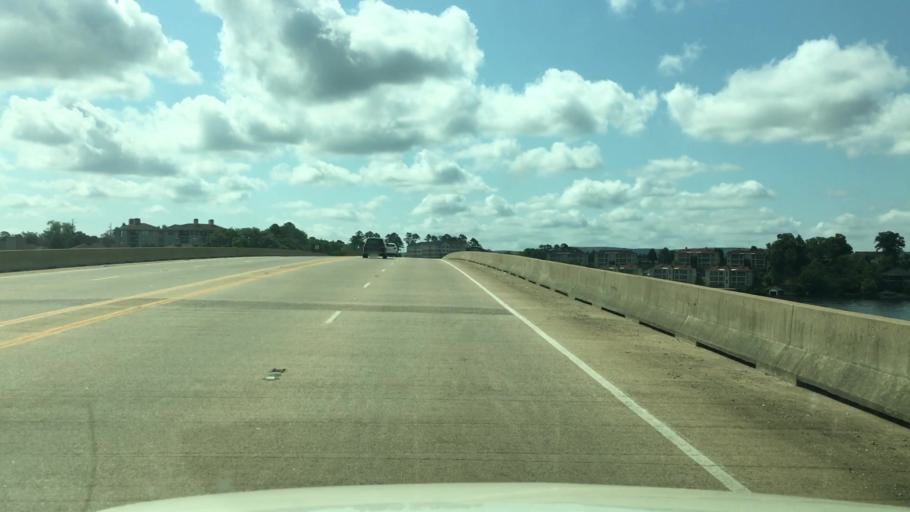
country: US
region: Arkansas
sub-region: Garland County
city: Lake Hamilton
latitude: 34.4340
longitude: -93.0882
